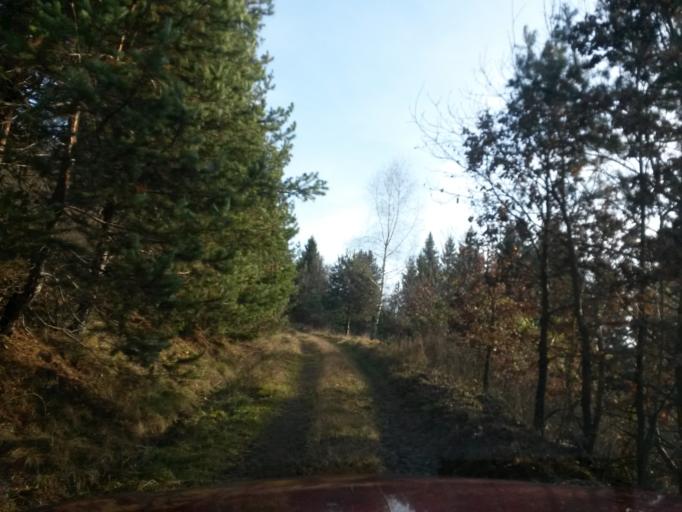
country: SK
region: Kosicky
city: Dobsina
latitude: 48.7263
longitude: 20.3816
